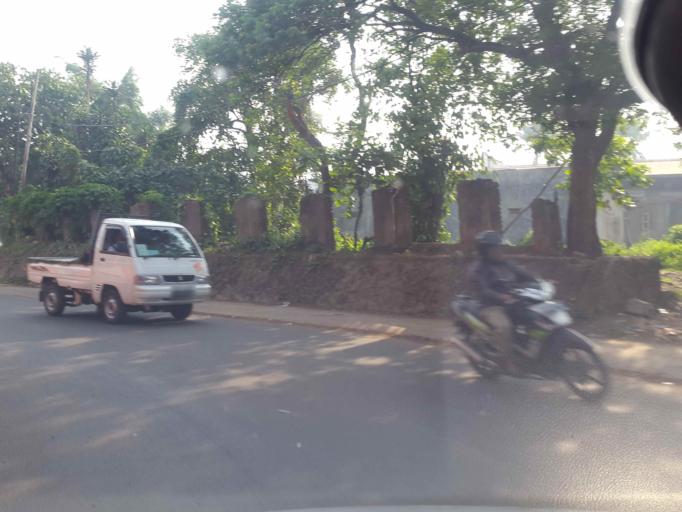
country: ID
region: West Java
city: Bekasi
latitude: -6.3142
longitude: 106.9926
